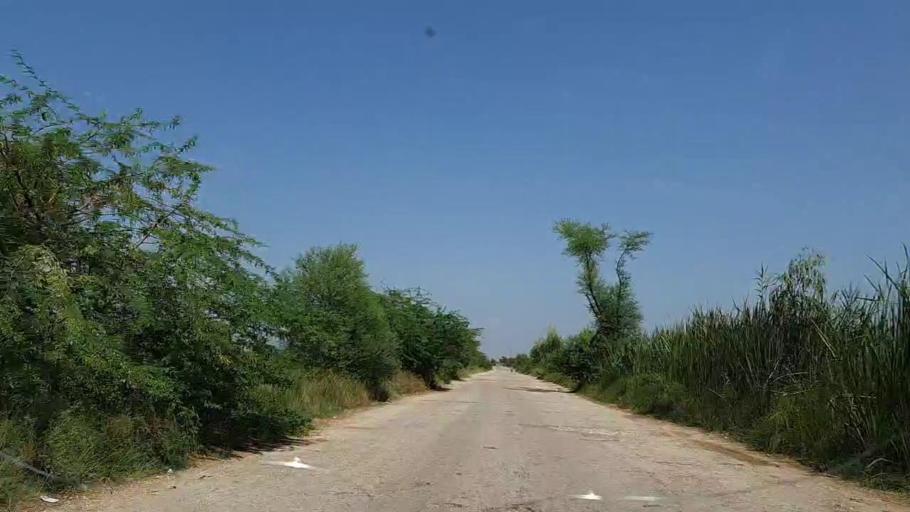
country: PK
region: Sindh
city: Naushahro Firoz
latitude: 26.8180
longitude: 68.1761
